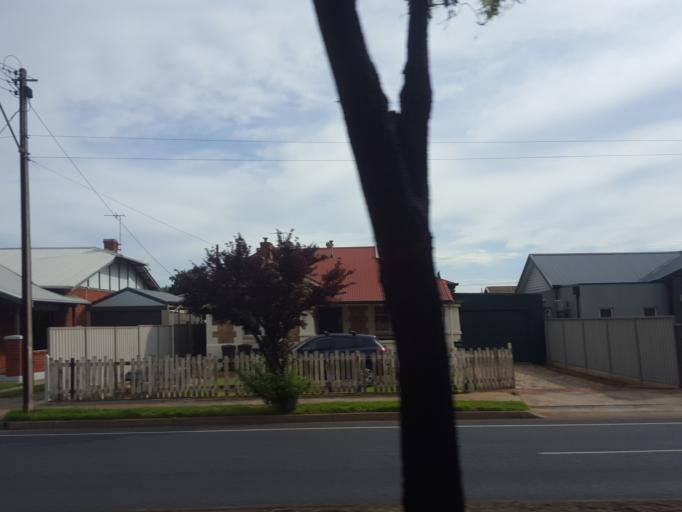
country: AU
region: South Australia
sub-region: Charles Sturt
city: Woodville
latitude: -34.8804
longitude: 138.5570
